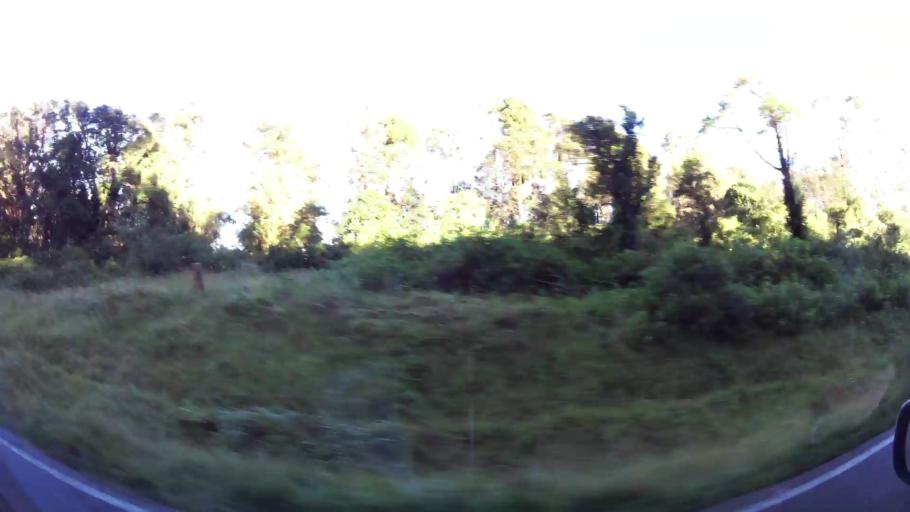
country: CR
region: San Jose
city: San Marcos
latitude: 9.6999
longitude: -83.9411
